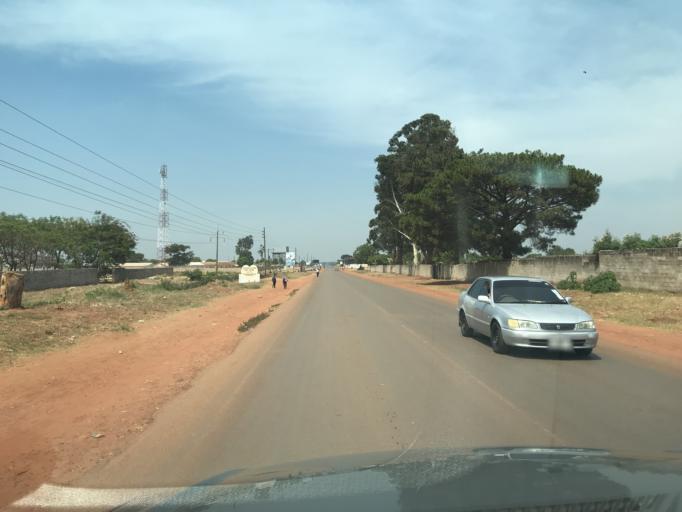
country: ZM
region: Northern
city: Kasama
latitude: -10.2069
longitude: 31.1748
